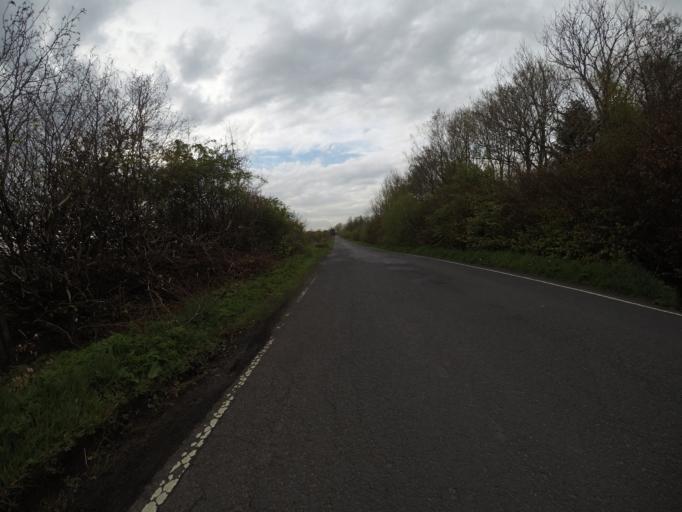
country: GB
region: Scotland
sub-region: East Ayrshire
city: Kilmarnock
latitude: 55.6431
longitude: -4.4802
